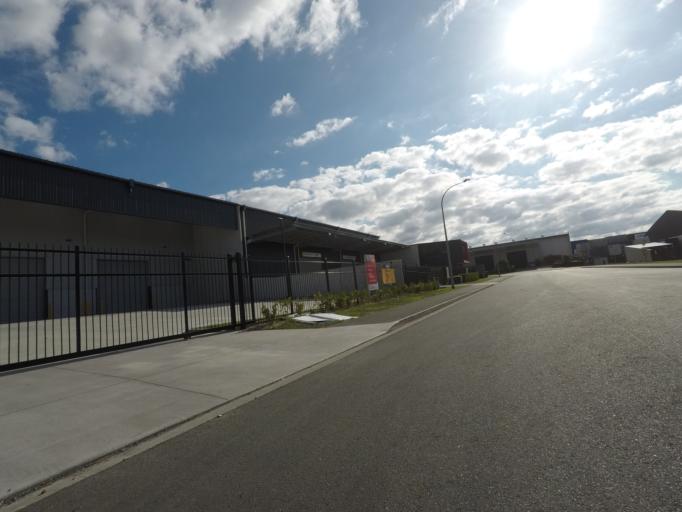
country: NZ
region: Auckland
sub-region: Auckland
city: Rosebank
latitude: -36.8823
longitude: 174.6849
